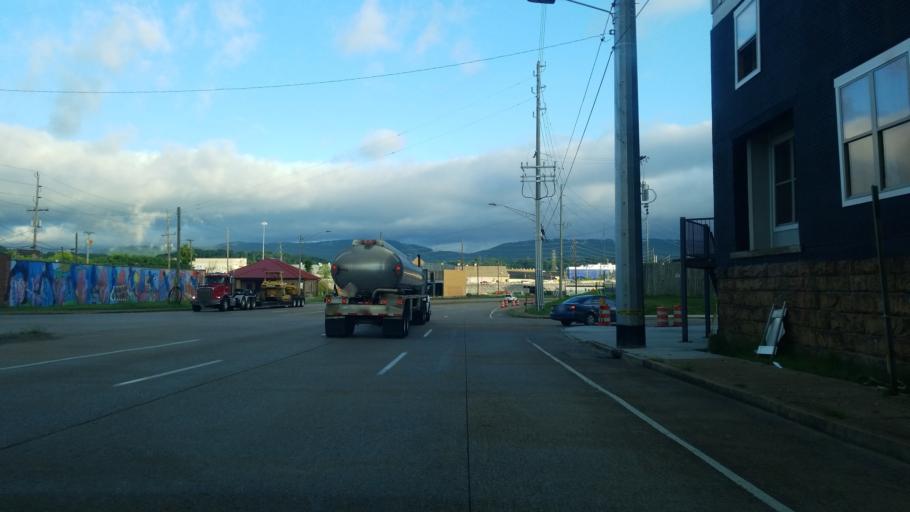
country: US
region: Tennessee
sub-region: Hamilton County
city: Chattanooga
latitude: 35.0341
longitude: -85.3153
